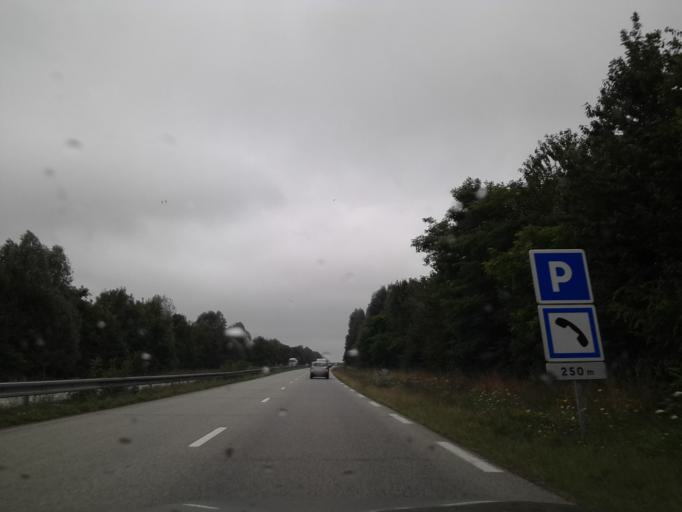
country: FR
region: Lower Normandy
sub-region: Departement de la Manche
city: Montebourg
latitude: 49.4793
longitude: -1.3812
